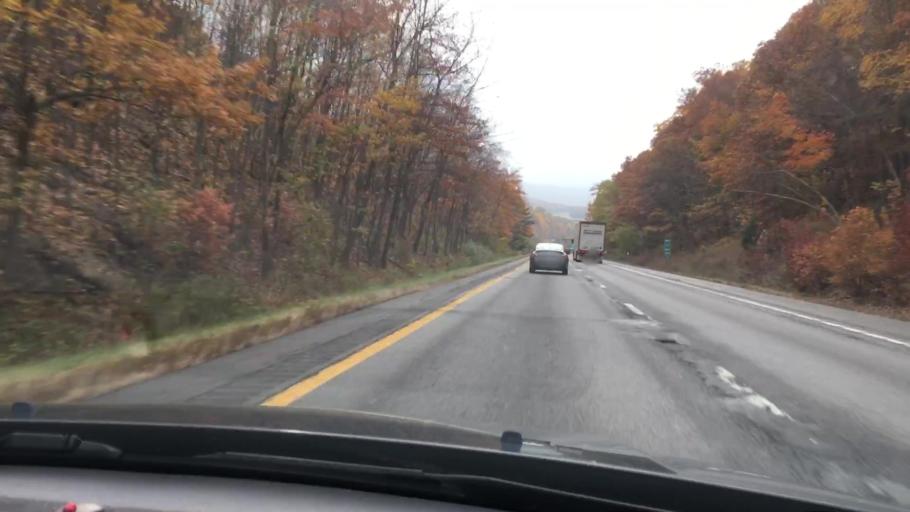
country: US
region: New York
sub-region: Dutchess County
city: Hillside Lake
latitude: 41.5465
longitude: -73.7470
